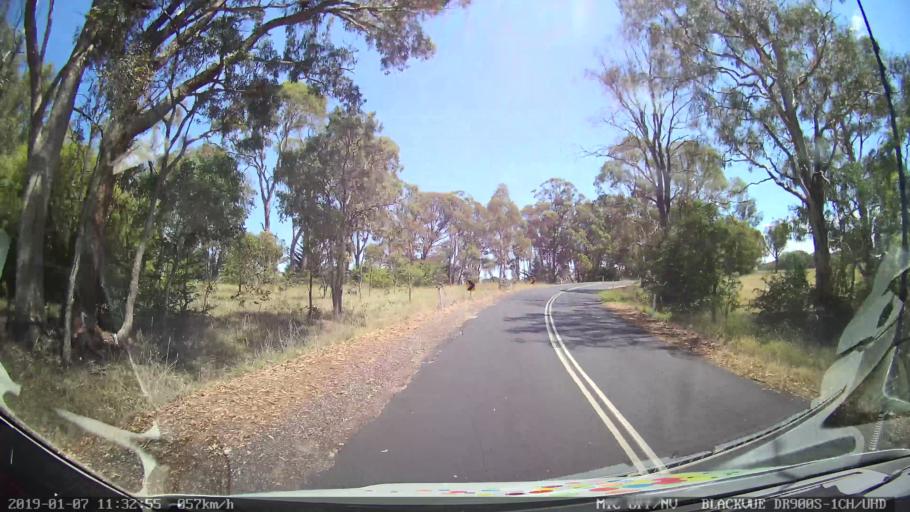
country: AU
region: New South Wales
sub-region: Armidale Dumaresq
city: Armidale
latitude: -30.4050
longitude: 151.5600
